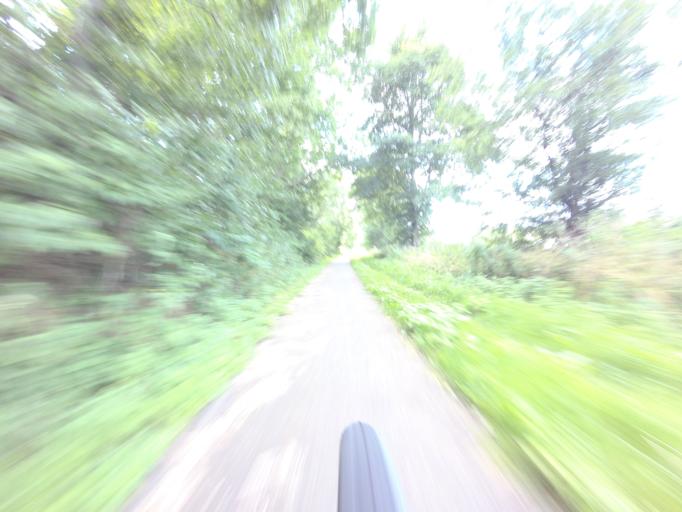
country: DK
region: Central Jutland
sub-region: Horsens Kommune
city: Horsens
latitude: 55.9396
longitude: 9.7797
